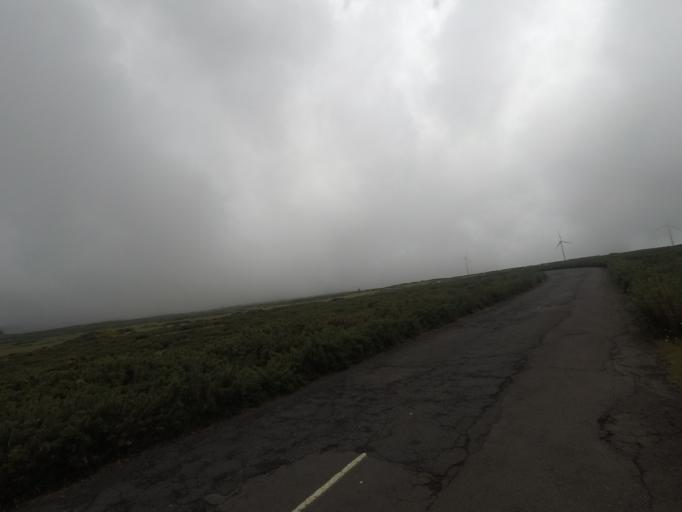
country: PT
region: Madeira
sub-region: Calheta
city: Arco da Calheta
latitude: 32.7537
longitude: -17.0987
